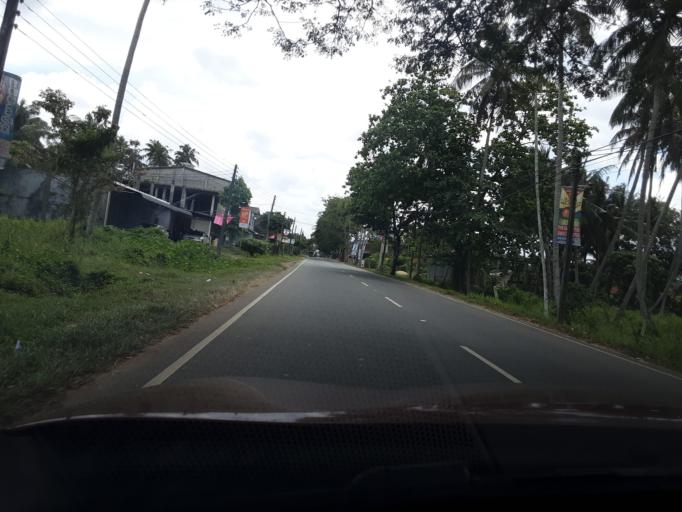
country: LK
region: North Western
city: Kuliyapitiya
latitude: 7.4518
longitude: 80.1660
